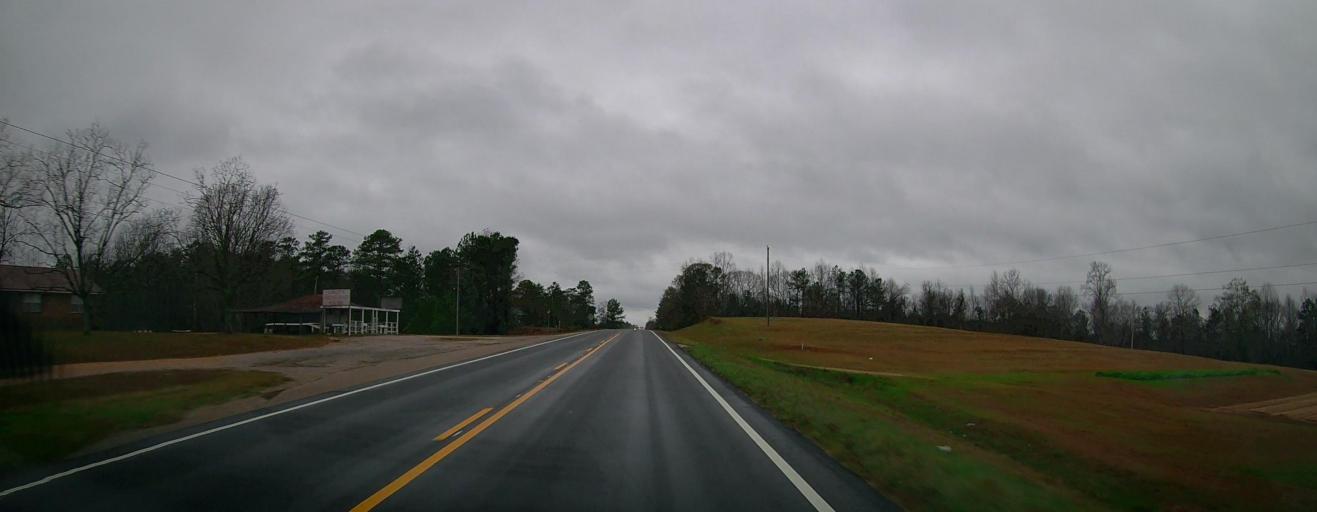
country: US
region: Alabama
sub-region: Chilton County
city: Thorsby
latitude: 32.8005
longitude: -86.9130
